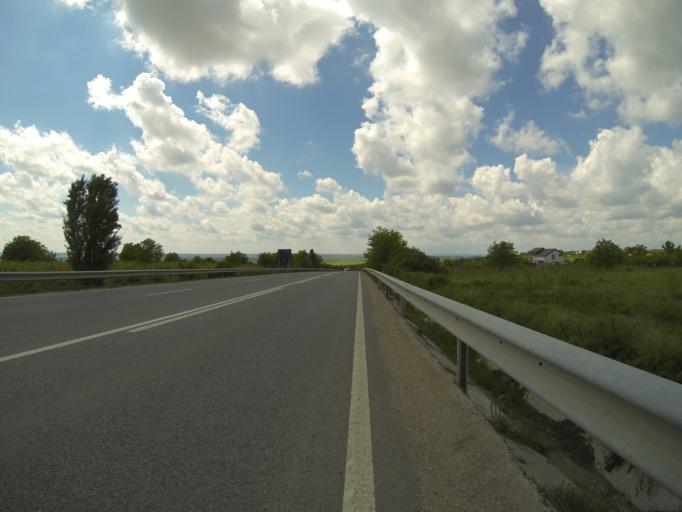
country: RO
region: Dolj
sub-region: Comuna Carcea
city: Carcea
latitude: 44.2651
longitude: 23.8964
